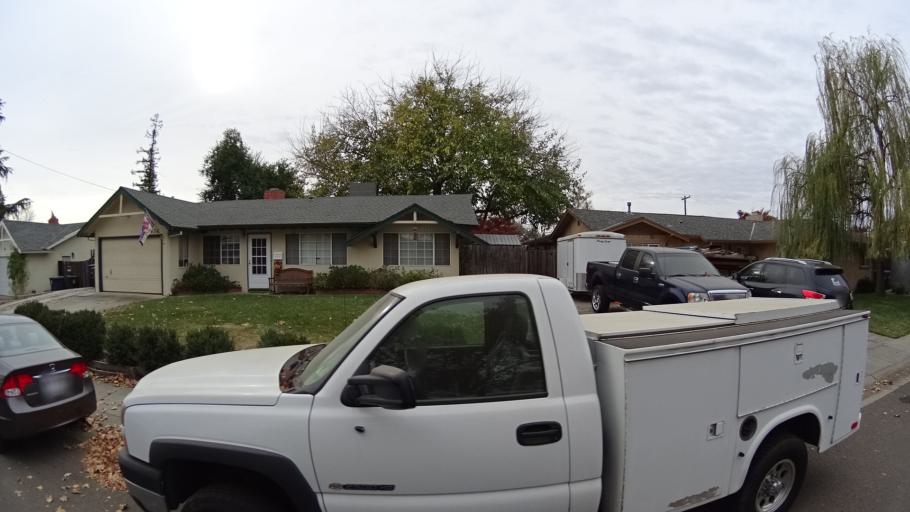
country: US
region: California
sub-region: Sacramento County
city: Citrus Heights
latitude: 38.7113
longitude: -121.2946
